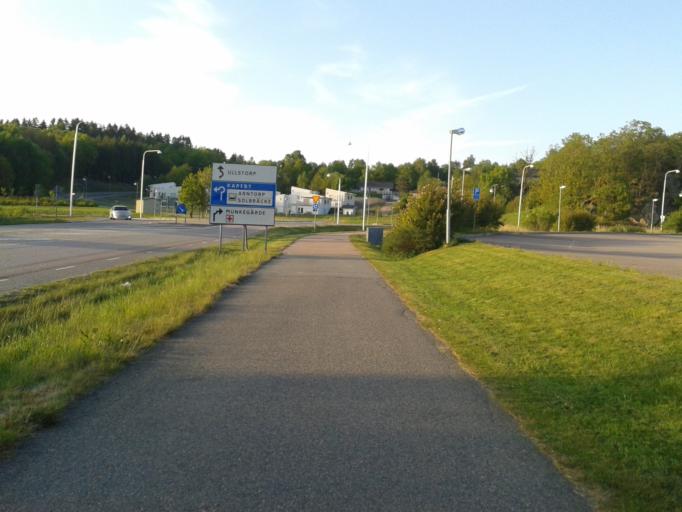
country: SE
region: Vaestra Goetaland
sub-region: Kungalvs Kommun
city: Kungalv
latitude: 57.8884
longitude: 11.9487
